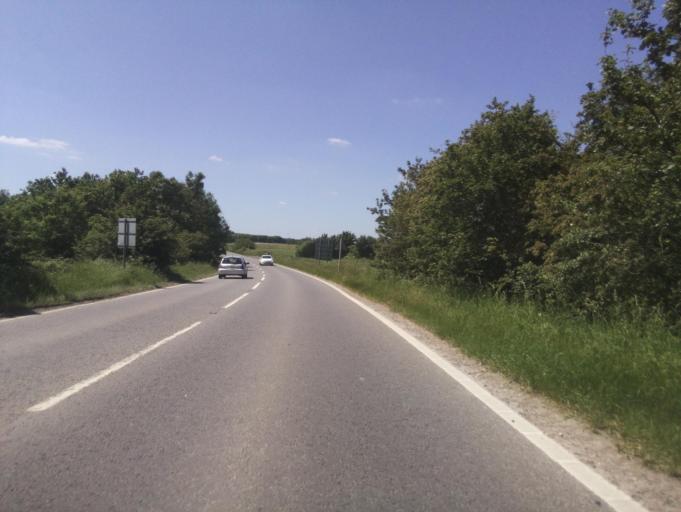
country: GB
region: England
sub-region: Wiltshire
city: Lydiard Tregoze
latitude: 51.5412
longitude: -1.8469
